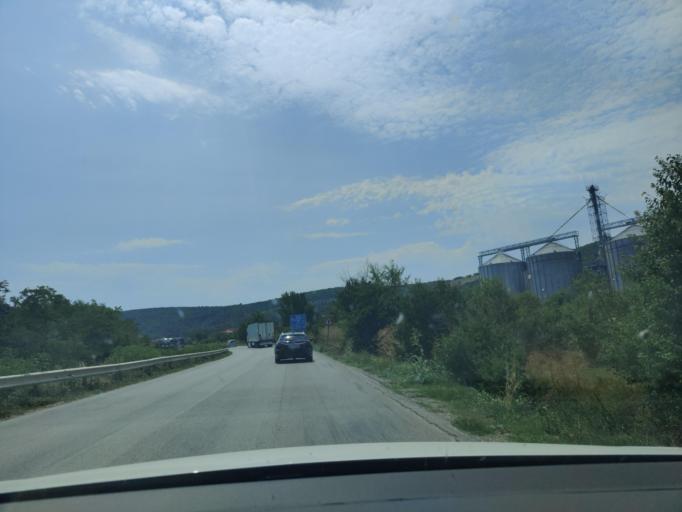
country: BG
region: Montana
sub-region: Obshtina Montana
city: Montana
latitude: 43.4498
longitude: 23.0976
